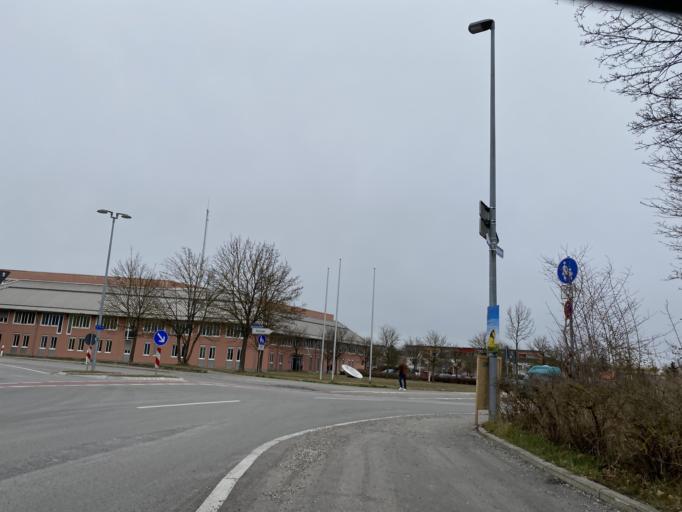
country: DE
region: Bavaria
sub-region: Upper Bavaria
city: Fuerstenfeldbruck
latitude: 48.1814
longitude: 11.2454
